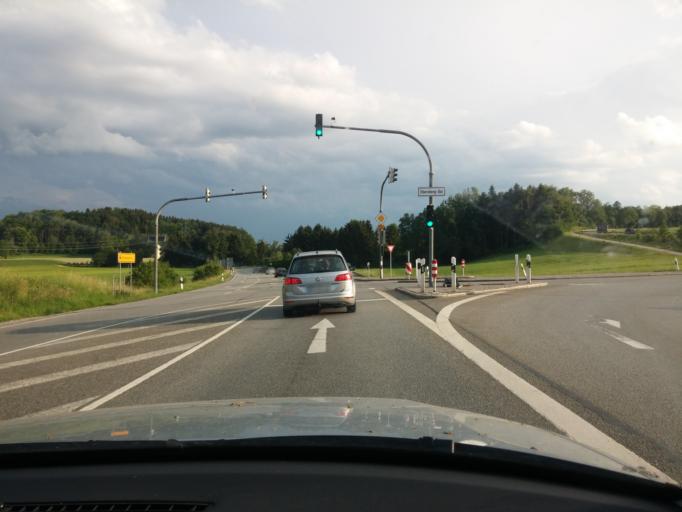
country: DE
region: Bavaria
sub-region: Upper Bavaria
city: Ebersberg
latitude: 48.0774
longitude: 11.9819
